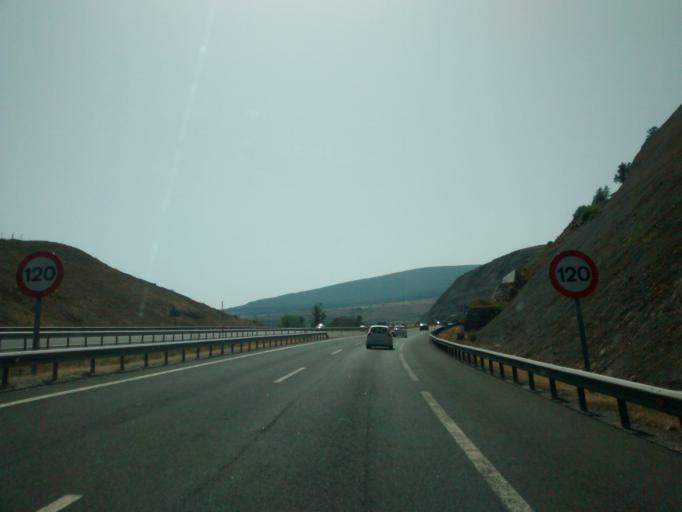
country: ES
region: Cantabria
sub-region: Provincia de Cantabria
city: Villaescusa
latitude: 42.9493
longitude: -4.1394
